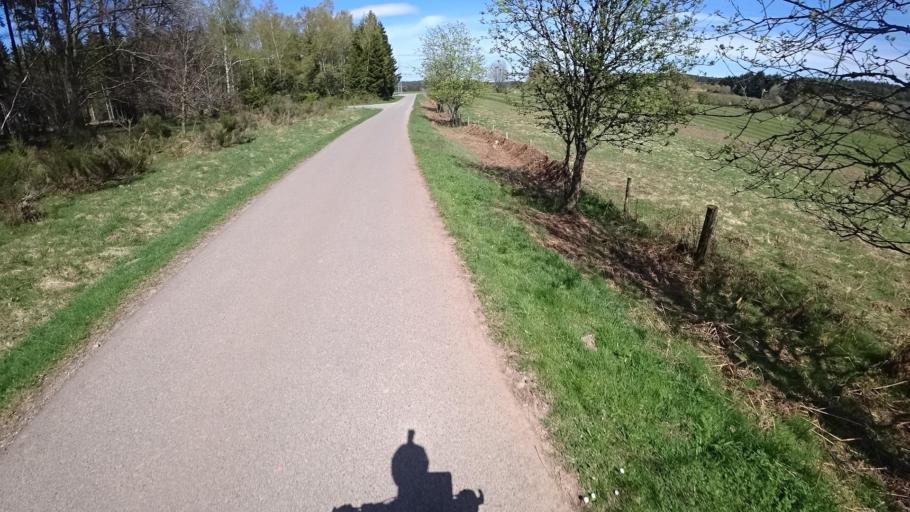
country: DE
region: Rheinland-Pfalz
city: Gusenburg
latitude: 49.6395
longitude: 6.8873
